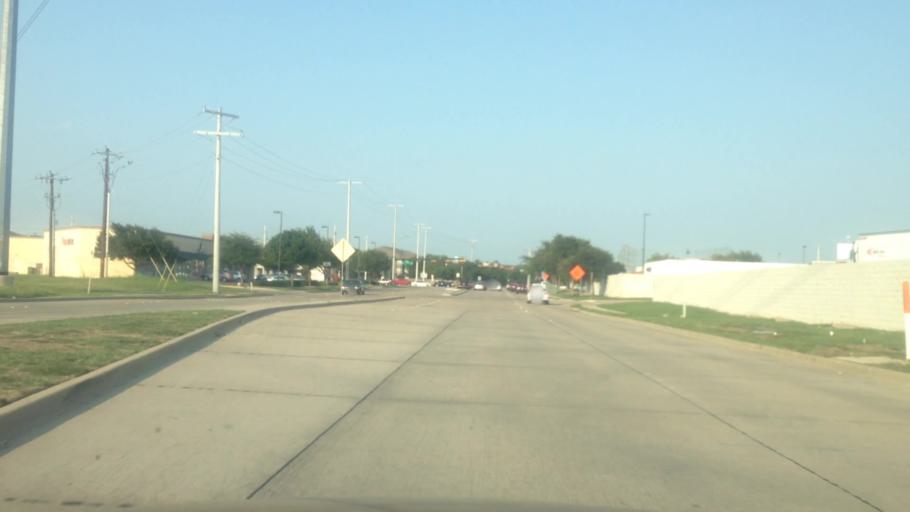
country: US
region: Texas
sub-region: Denton County
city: The Colony
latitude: 33.0678
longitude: -96.8932
